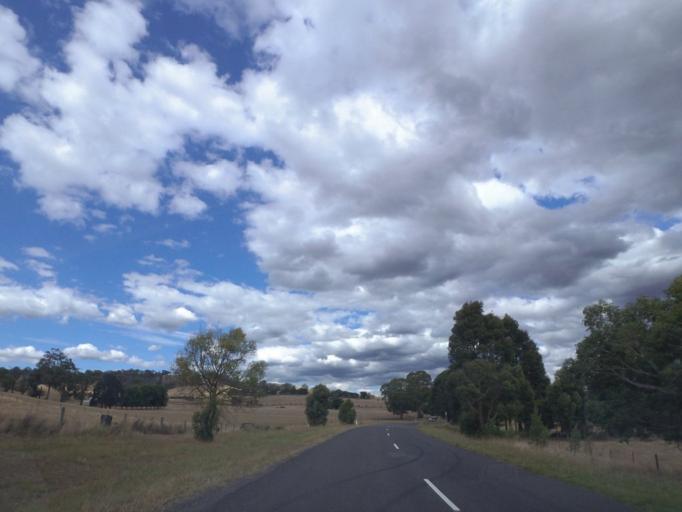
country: AU
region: Victoria
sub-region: Yarra Ranges
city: Yarra Glen
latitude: -37.6382
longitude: 145.4446
